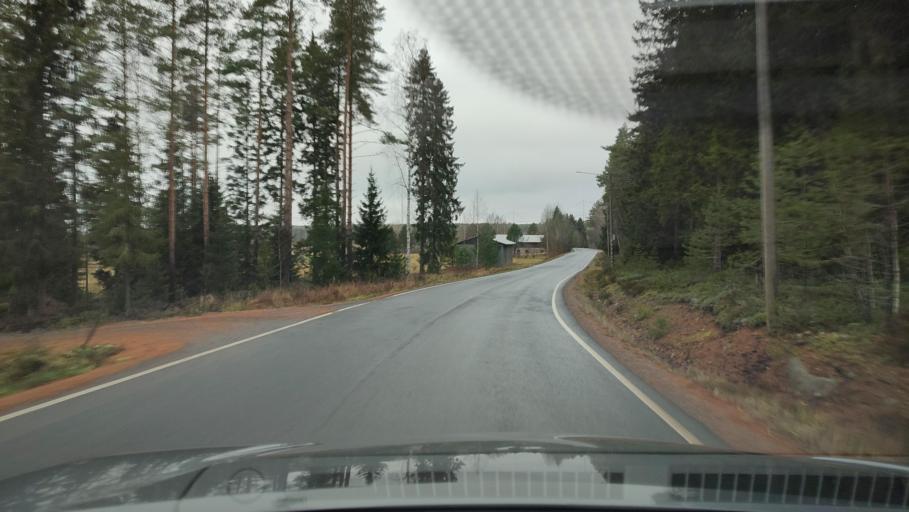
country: FI
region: Southern Ostrobothnia
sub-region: Suupohja
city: Karijoki
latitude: 62.1399
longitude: 21.6850
